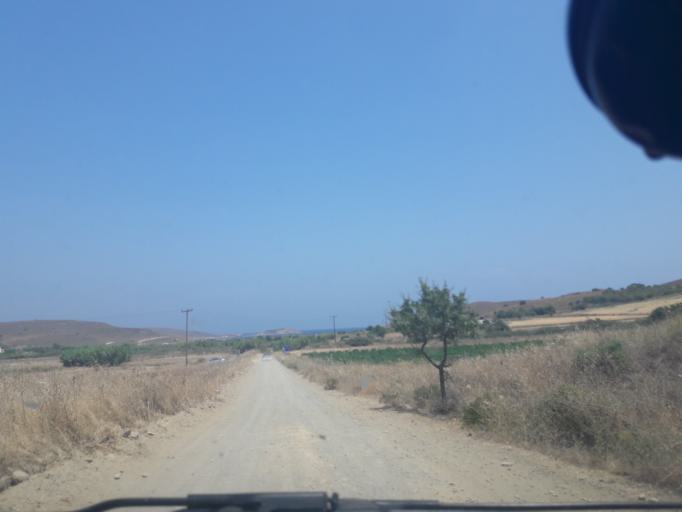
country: GR
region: North Aegean
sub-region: Nomos Lesvou
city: Myrina
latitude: 39.9784
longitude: 25.1500
